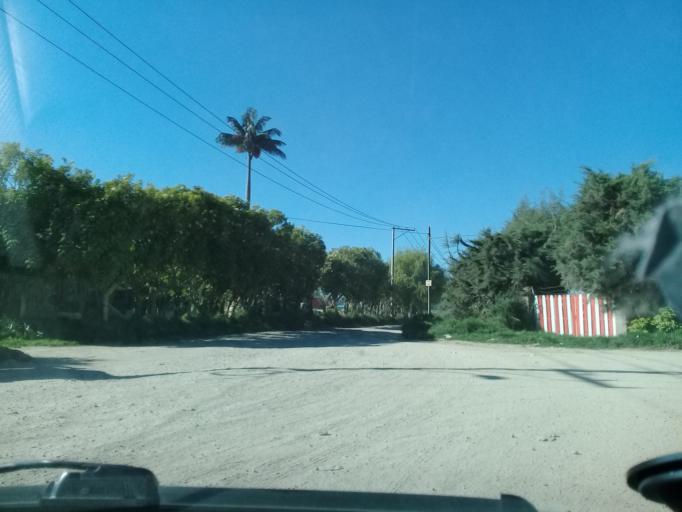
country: CO
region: Cundinamarca
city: Funza
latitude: 4.7427
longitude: -74.2271
